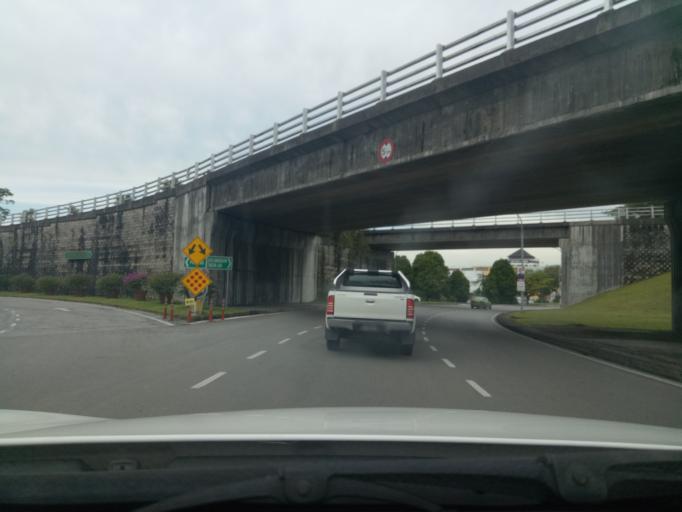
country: MY
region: Sarawak
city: Kuching
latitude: 1.5310
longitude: 110.3600
